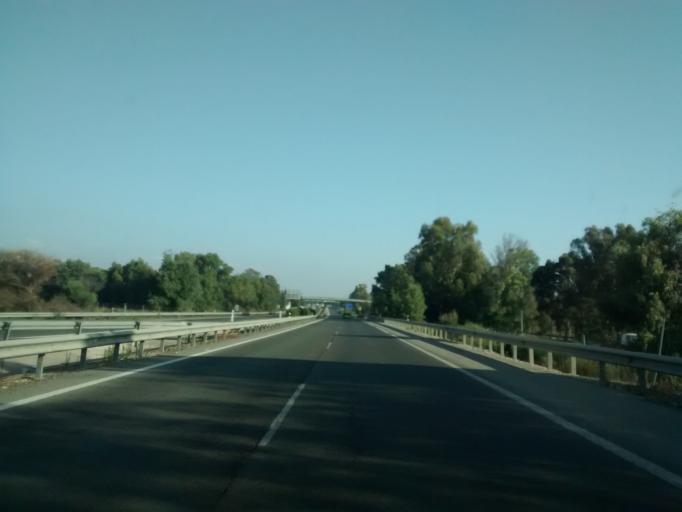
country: ES
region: Andalusia
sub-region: Provincia de Cadiz
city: Chiclana de la Frontera
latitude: 36.3962
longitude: -6.1240
